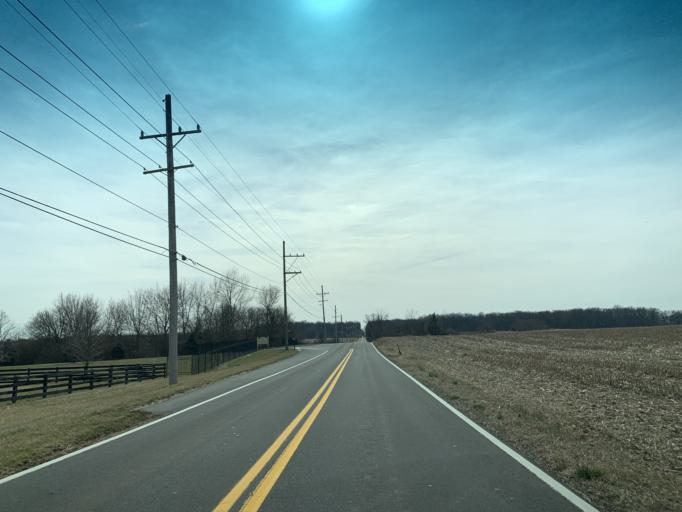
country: US
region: Maryland
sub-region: Frederick County
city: Buckeystown
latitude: 39.3393
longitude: -77.4523
